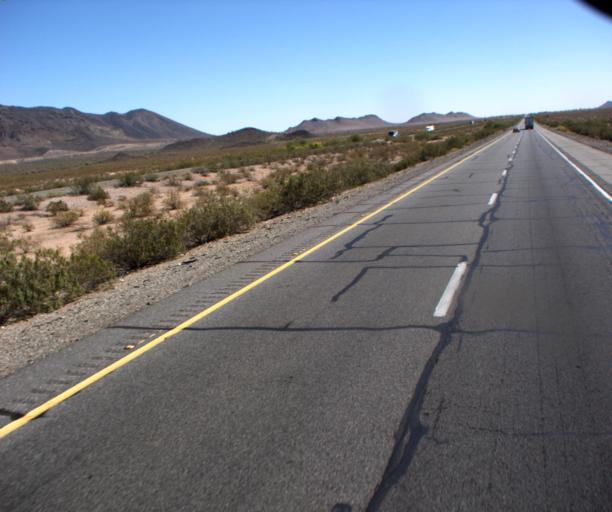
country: US
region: Arizona
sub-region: Maricopa County
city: Buckeye
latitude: 33.5263
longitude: -113.1052
